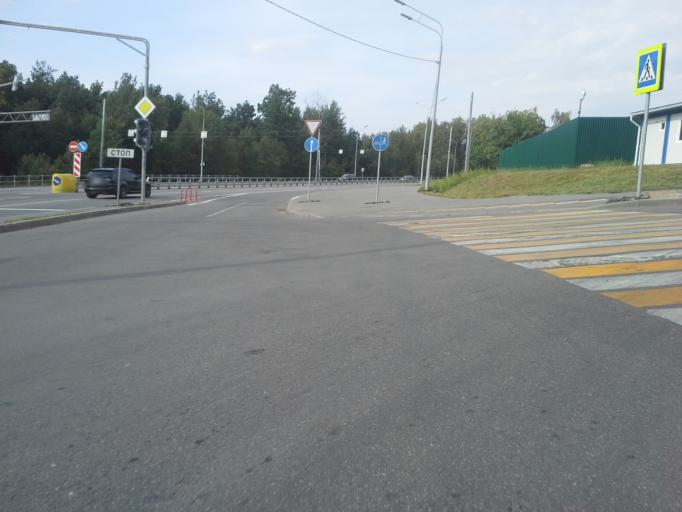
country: RU
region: Moskovskaya
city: Kokoshkino
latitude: 55.6001
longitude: 37.1598
